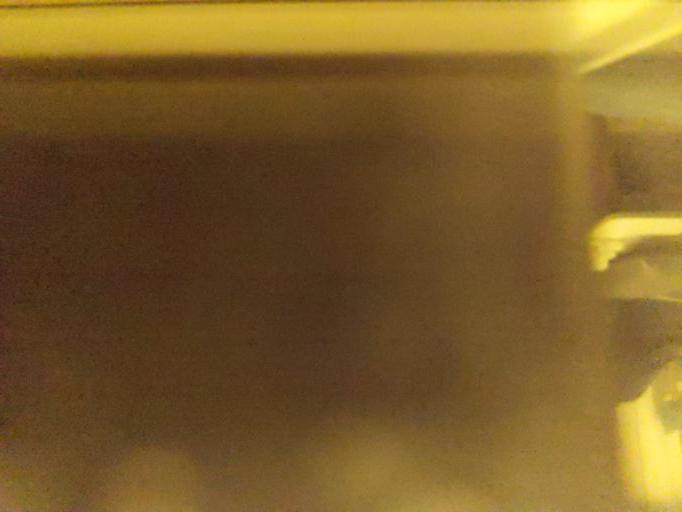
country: JP
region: Shizuoka
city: Atami
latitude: 35.1152
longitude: 139.0830
